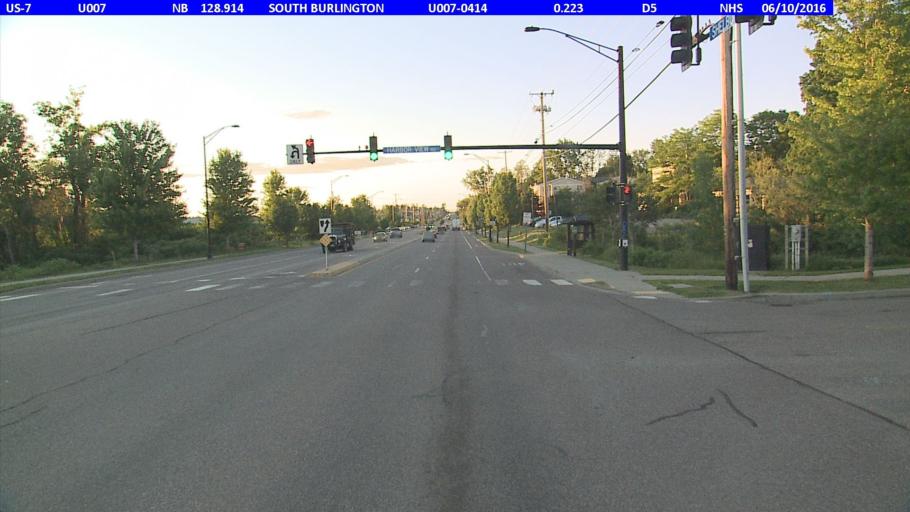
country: US
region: Vermont
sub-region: Chittenden County
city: Burlington
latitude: 44.4240
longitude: -73.2117
